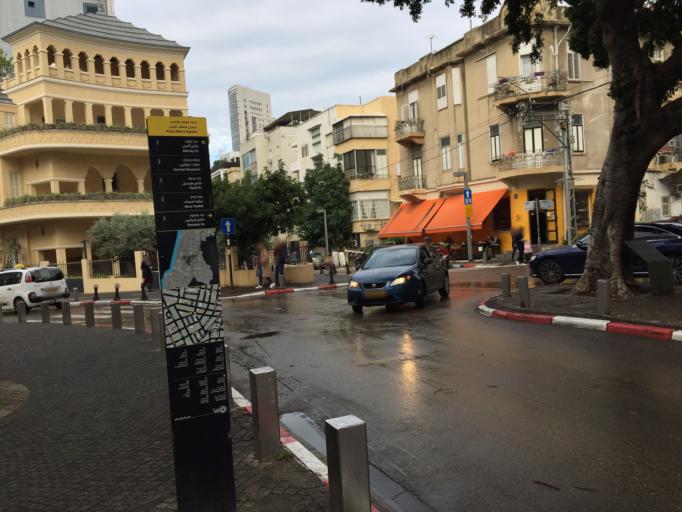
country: IL
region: Tel Aviv
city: Tel Aviv
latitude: 32.0657
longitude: 34.7748
